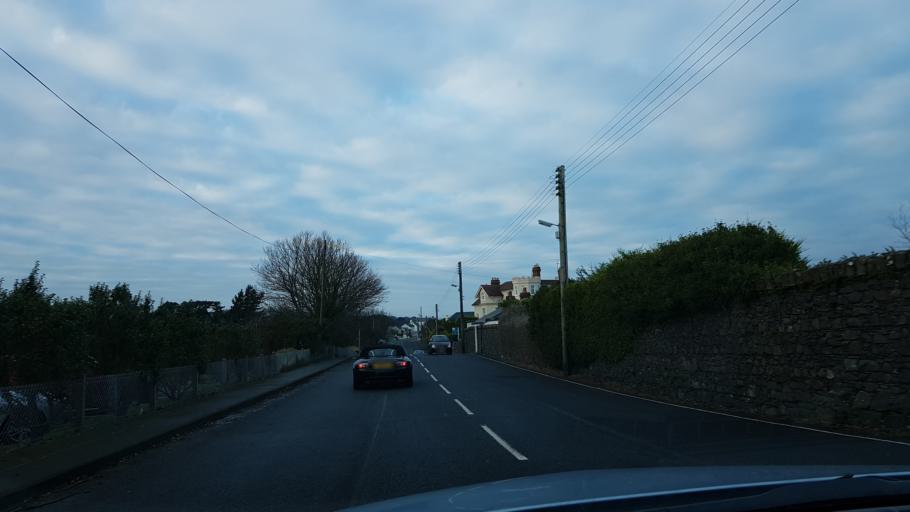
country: GB
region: Northern Ireland
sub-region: Down District
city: Donaghadee
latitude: 54.6538
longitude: -5.5488
